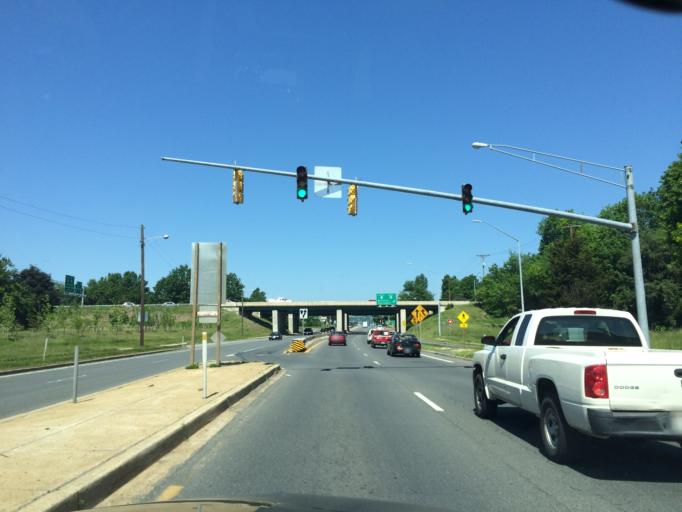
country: US
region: Maryland
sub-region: Frederick County
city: Frederick
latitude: 39.4150
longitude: -77.4330
